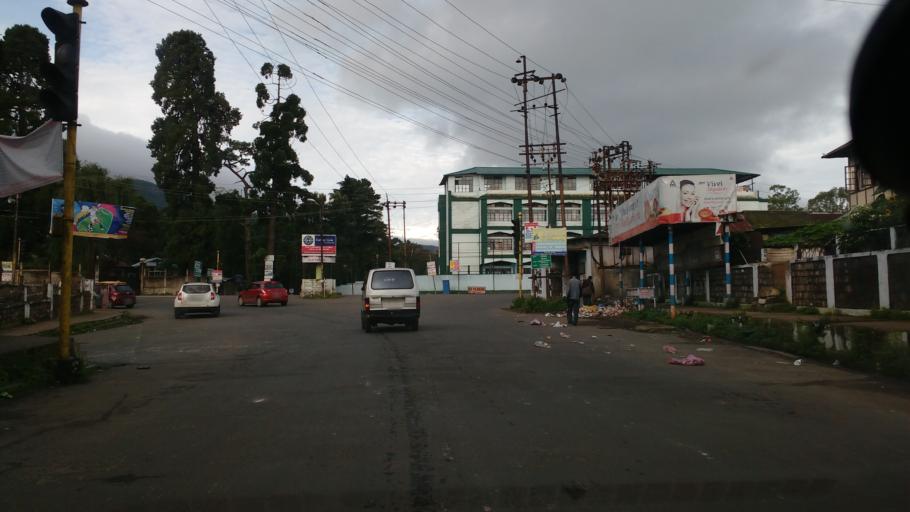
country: IN
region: Meghalaya
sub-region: East Khasi Hills
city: Shillong
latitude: 25.5673
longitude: 91.8833
